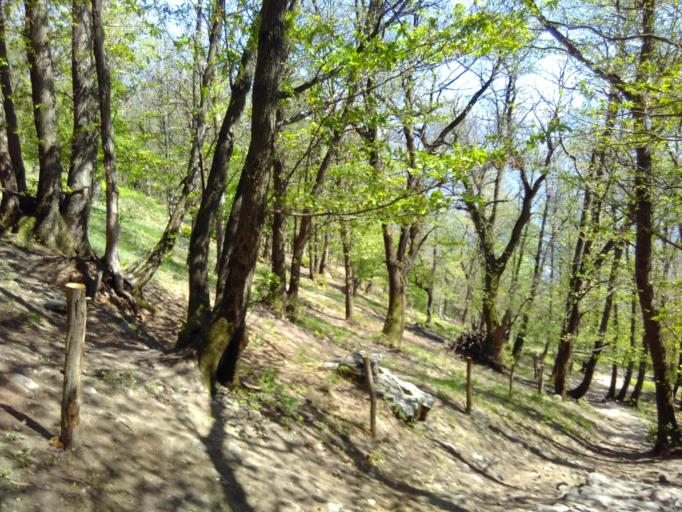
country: CH
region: Ticino
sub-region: Bellinzona District
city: Sementina
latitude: 46.1963
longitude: 8.9818
